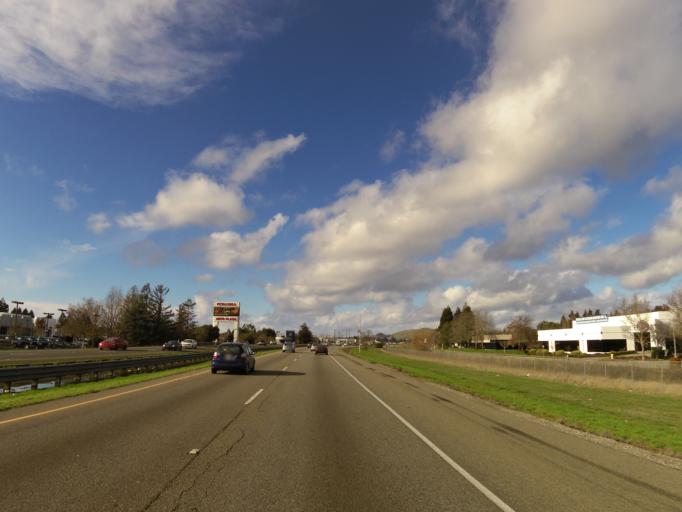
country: US
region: California
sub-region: Sonoma County
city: Penngrove
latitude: 38.2647
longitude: -122.6605
